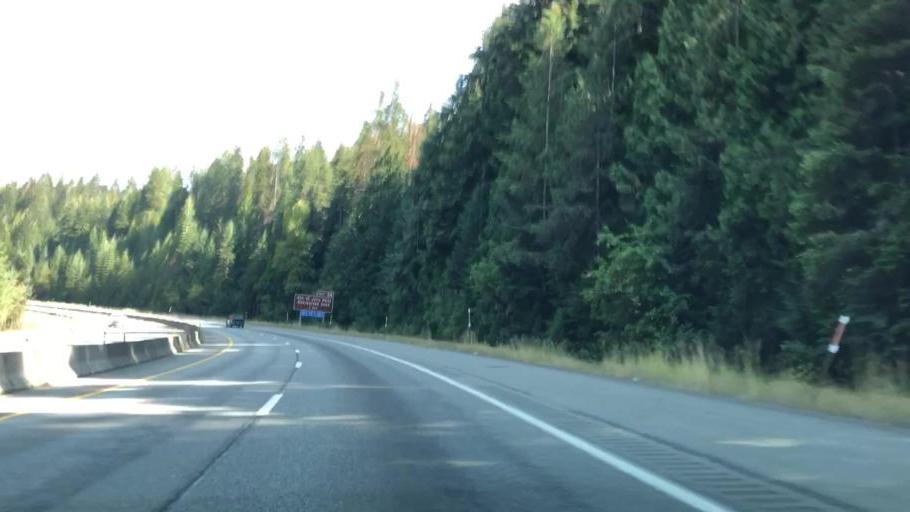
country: US
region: Idaho
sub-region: Kootenai County
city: Coeur d'Alene
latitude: 47.6225
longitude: -116.5581
